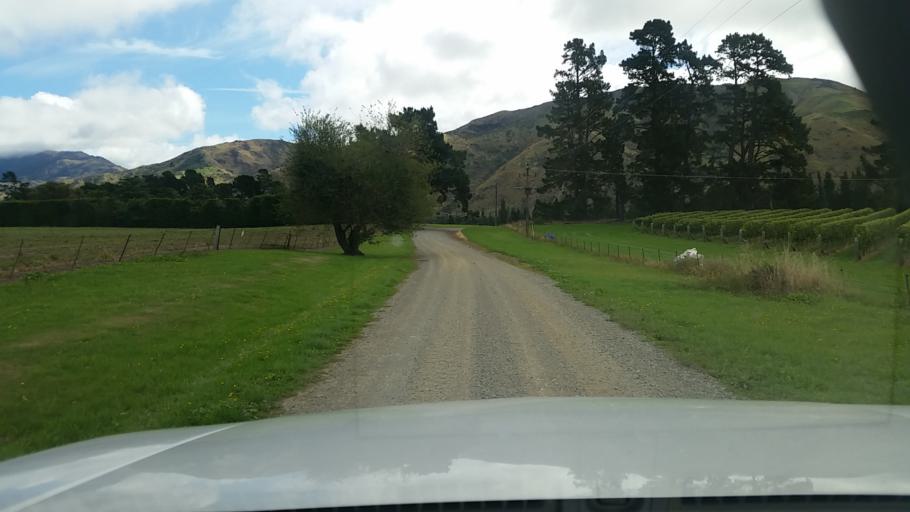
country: NZ
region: Marlborough
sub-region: Marlborough District
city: Blenheim
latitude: -41.6963
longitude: 173.9493
